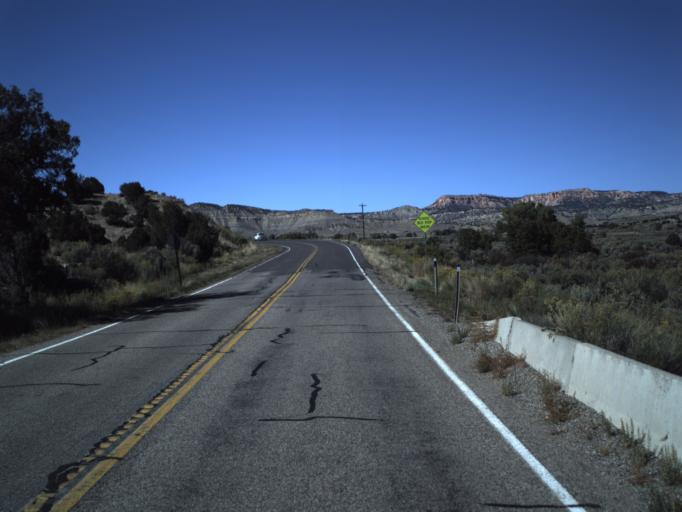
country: US
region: Utah
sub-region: Garfield County
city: Panguitch
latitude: 37.6101
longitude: -112.0619
